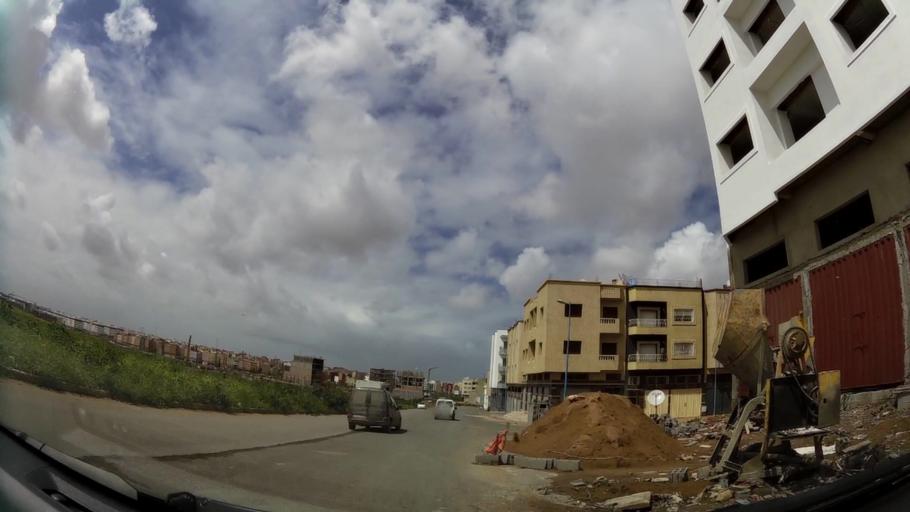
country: MA
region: Grand Casablanca
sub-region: Casablanca
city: Casablanca
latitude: 33.5257
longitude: -7.6016
